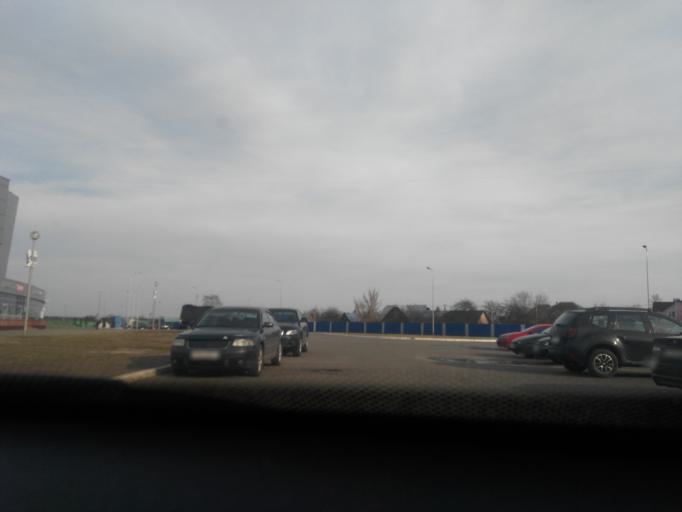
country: BY
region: Gomel
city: Zhlobin
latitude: 52.9086
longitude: 30.0500
